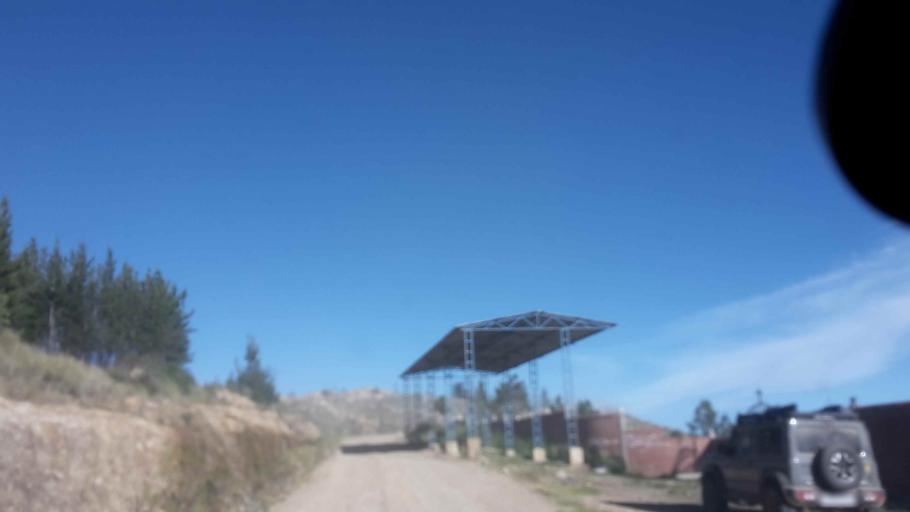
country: BO
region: Cochabamba
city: Arani
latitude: -17.7127
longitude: -65.6886
